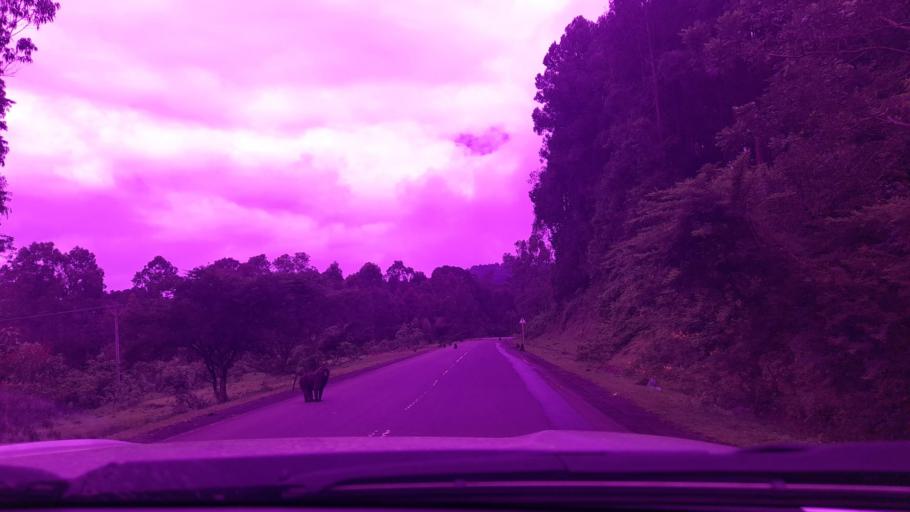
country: ET
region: Oromiya
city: Jima
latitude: 7.5521
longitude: 36.5863
